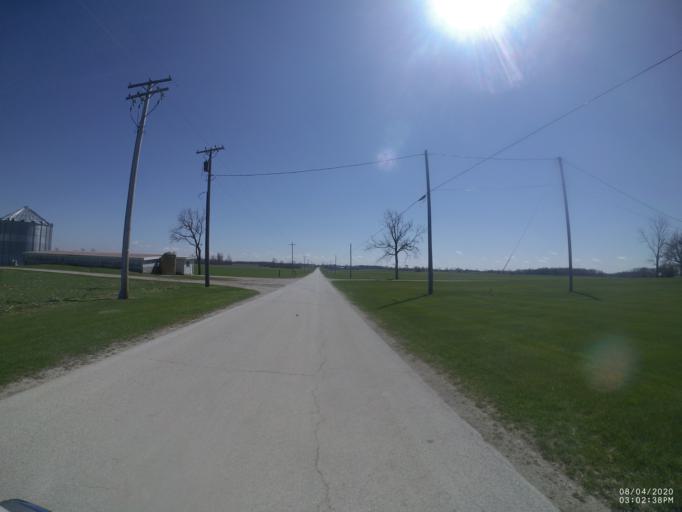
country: US
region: Ohio
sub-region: Sandusky County
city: Stony Prairie
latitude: 41.3362
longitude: -83.2395
